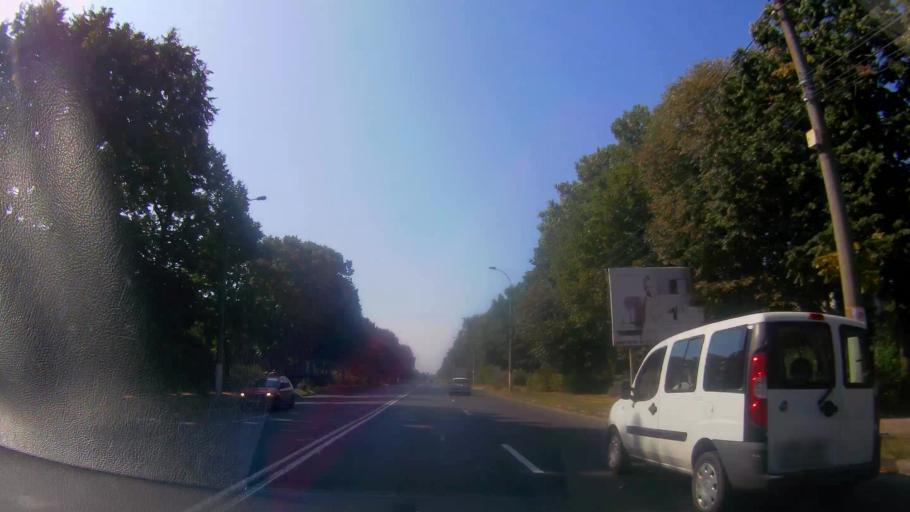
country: RO
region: Giurgiu
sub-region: Comuna Fratesti
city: Remus
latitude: 43.9263
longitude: 25.9747
